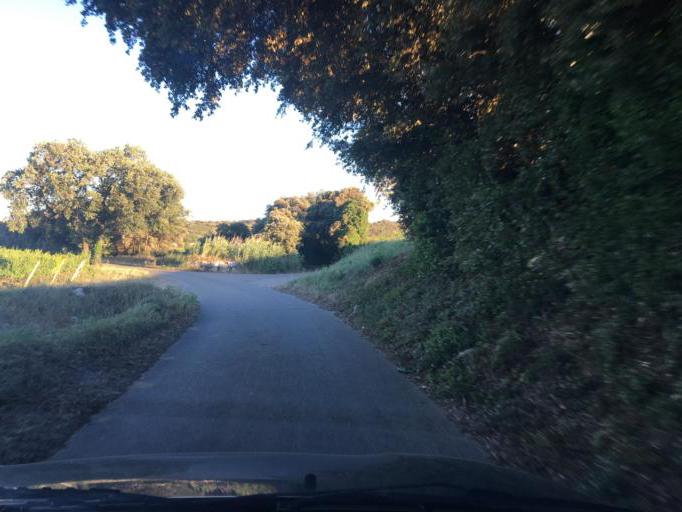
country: FR
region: Provence-Alpes-Cote d'Azur
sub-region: Departement du Vaucluse
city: Chateauneuf-du-Pape
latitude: 44.0766
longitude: 4.8251
